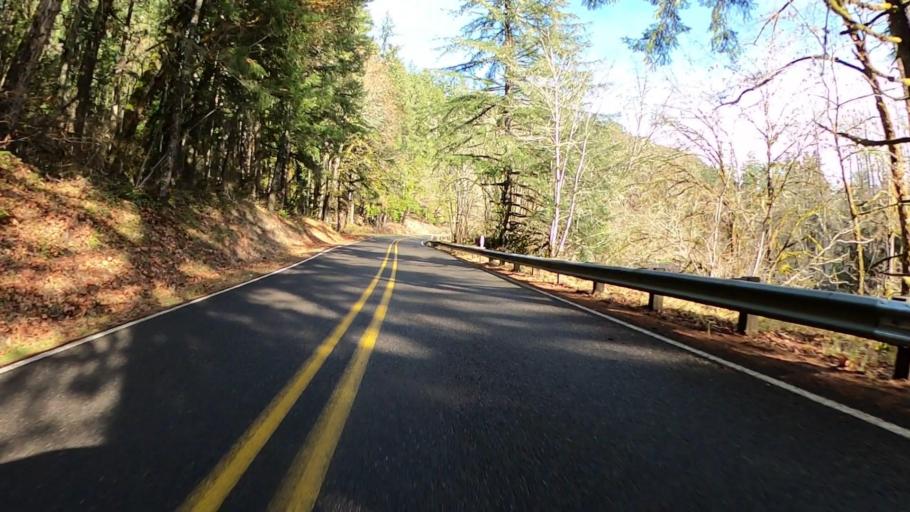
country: US
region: Oregon
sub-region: Lane County
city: Oakridge
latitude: 43.7483
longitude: -122.5139
